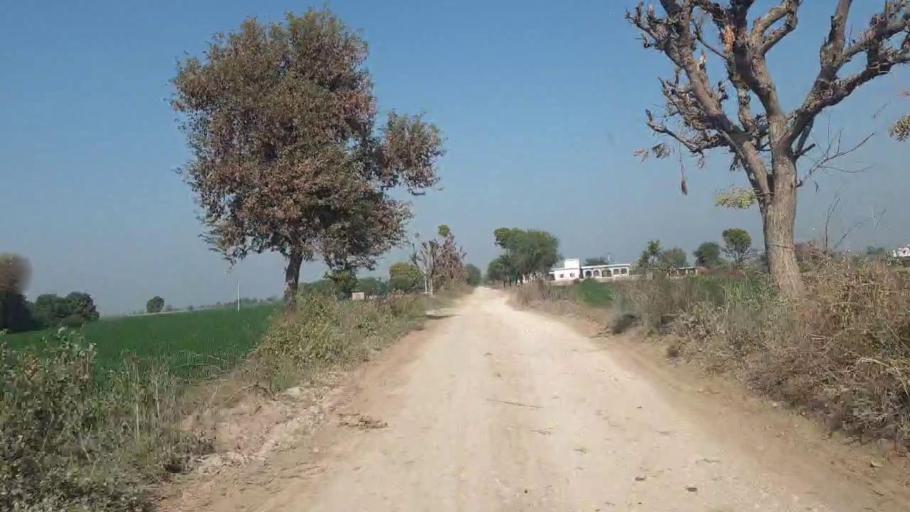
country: PK
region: Sindh
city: Sakrand
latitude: 26.0449
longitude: 68.4338
